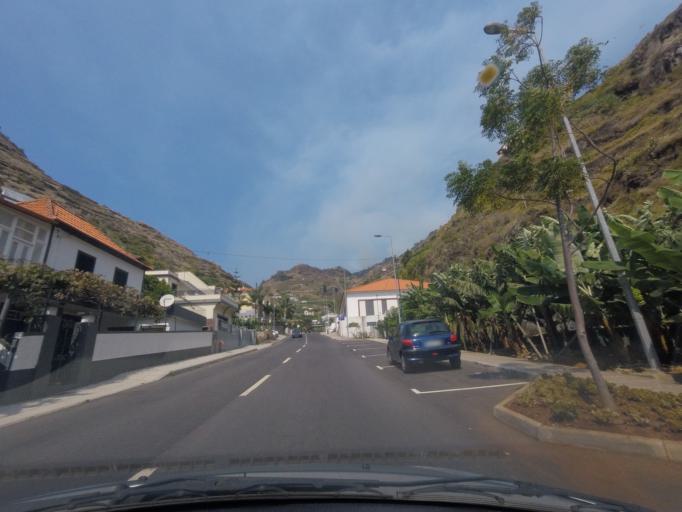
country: PT
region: Madeira
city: Ponta do Sol
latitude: 32.6807
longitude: -17.0765
